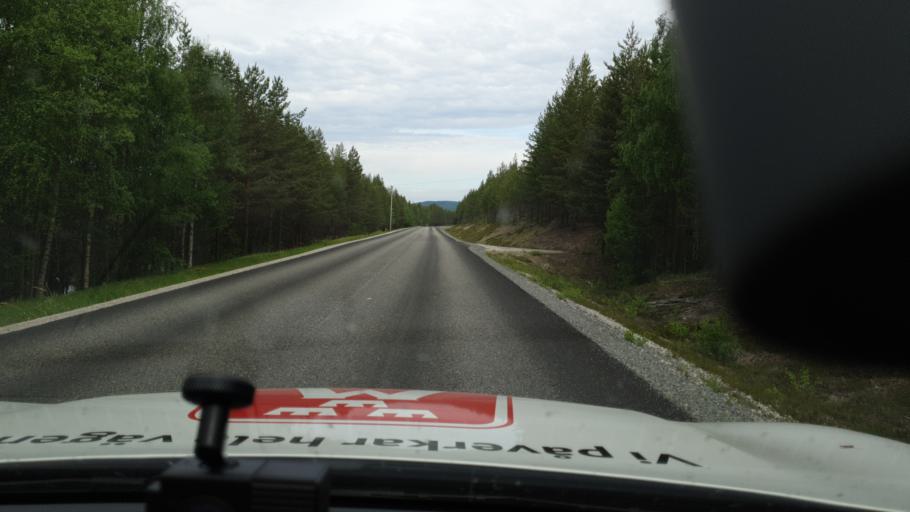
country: SE
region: Vaesterbotten
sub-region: Mala Kommun
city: Mala
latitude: 64.9167
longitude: 18.6402
